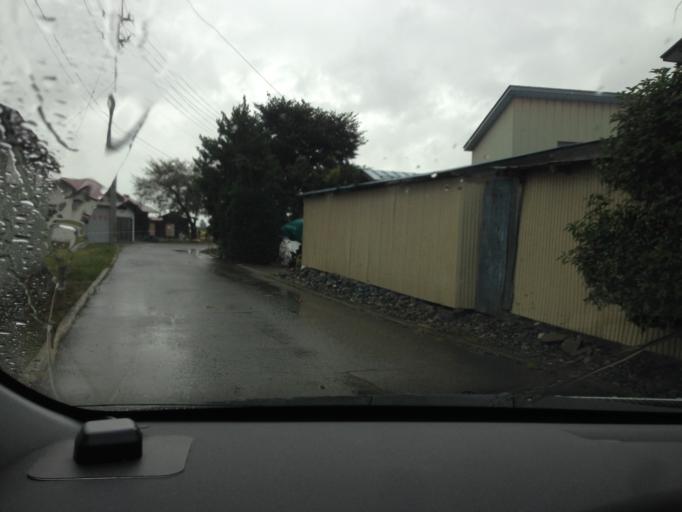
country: JP
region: Fukushima
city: Kitakata
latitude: 37.4632
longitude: 139.8650
